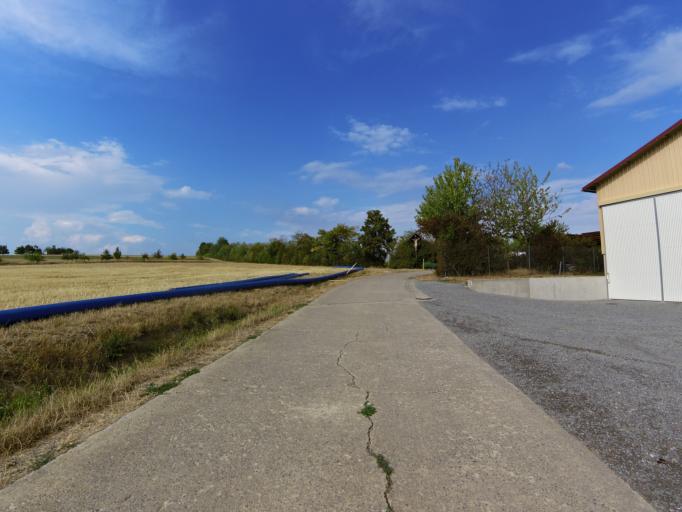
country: DE
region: Bavaria
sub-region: Regierungsbezirk Unterfranken
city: Hettstadt
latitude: 49.8053
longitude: 9.8179
